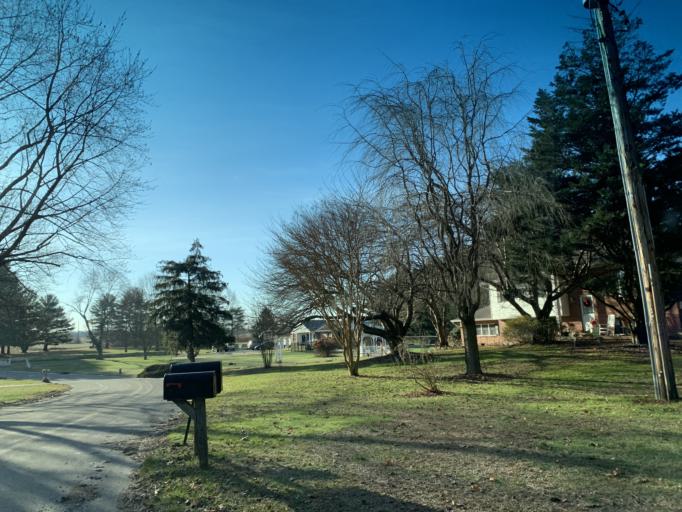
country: US
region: Maryland
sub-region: Harford County
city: Aberdeen
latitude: 39.5754
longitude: -76.1761
